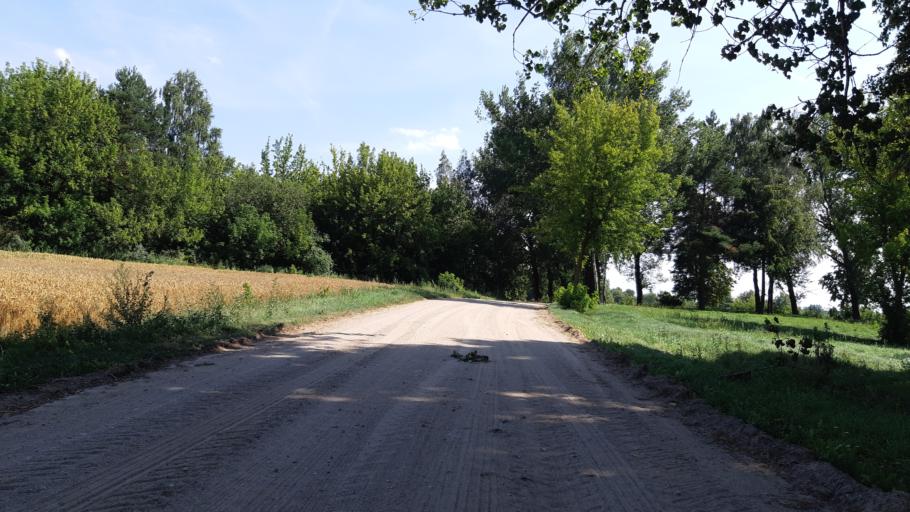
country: LT
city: Virbalis
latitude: 54.6359
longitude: 22.8248
